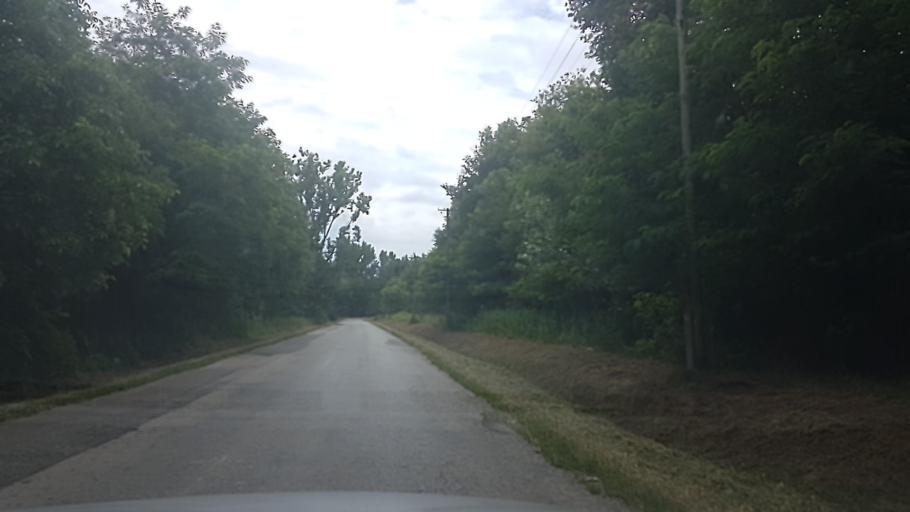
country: HU
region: Somogy
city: Barcs
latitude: 45.9684
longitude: 17.5891
